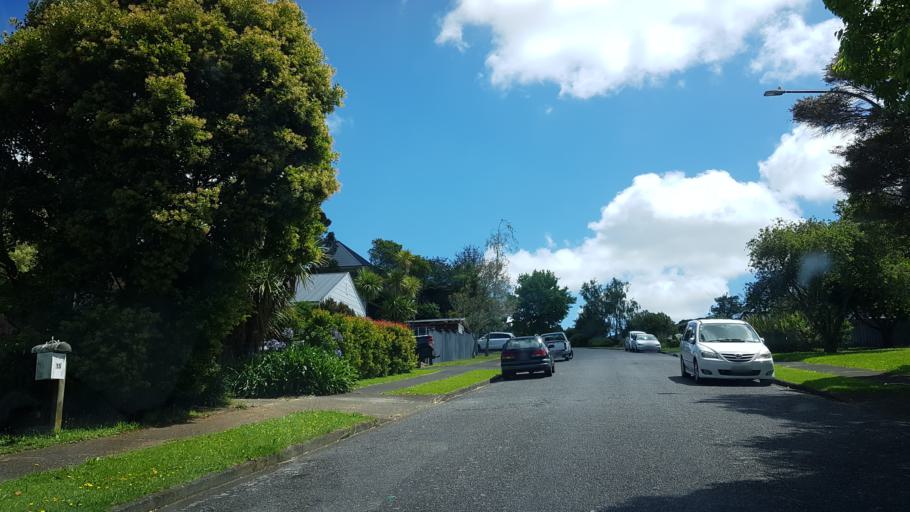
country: NZ
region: Auckland
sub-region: Auckland
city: North Shore
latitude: -36.7929
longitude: 174.7141
